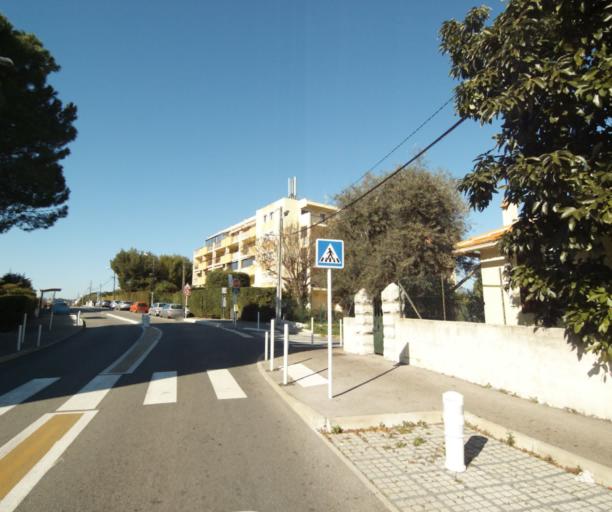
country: FR
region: Provence-Alpes-Cote d'Azur
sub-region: Departement des Alpes-Maritimes
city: Biot
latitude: 43.5971
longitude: 7.0976
